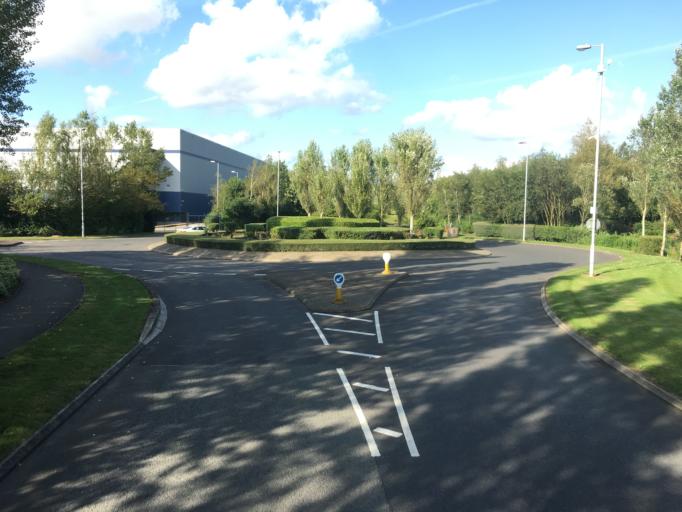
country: GB
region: England
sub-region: Leicestershire
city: Lutterworth
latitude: 52.4667
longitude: -1.2349
